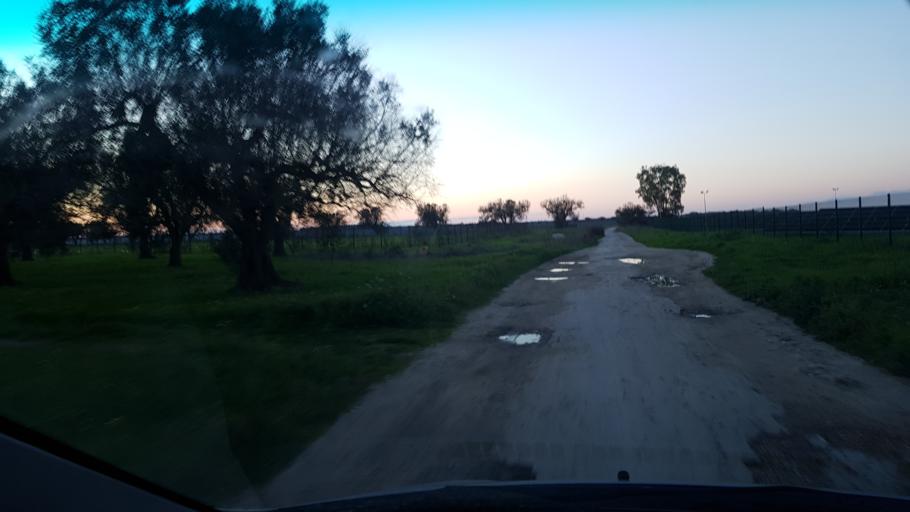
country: IT
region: Apulia
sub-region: Provincia di Brindisi
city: San Pietro Vernotico
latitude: 40.5070
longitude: 17.9731
